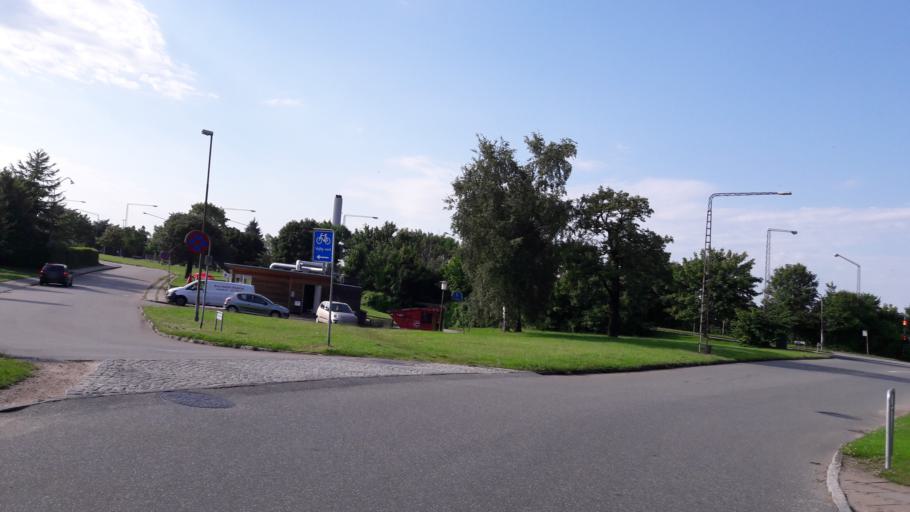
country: DK
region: Central Jutland
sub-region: Arhus Kommune
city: Arhus
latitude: 56.1958
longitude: 10.2177
